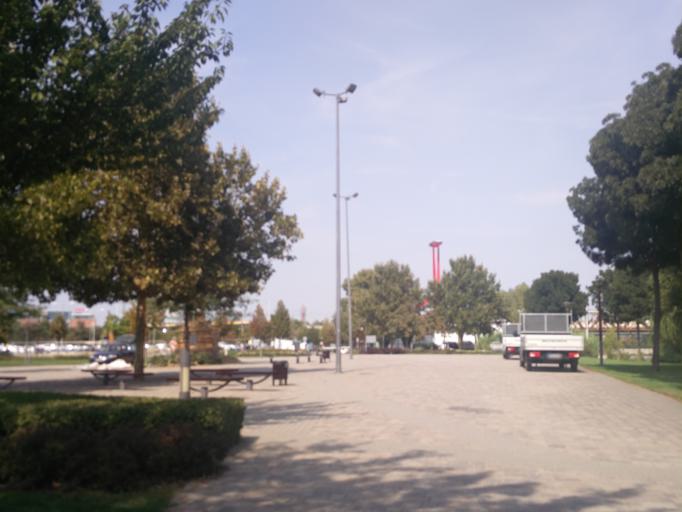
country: HU
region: Budapest
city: Budapest IX. keruelet
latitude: 47.4660
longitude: 19.0638
